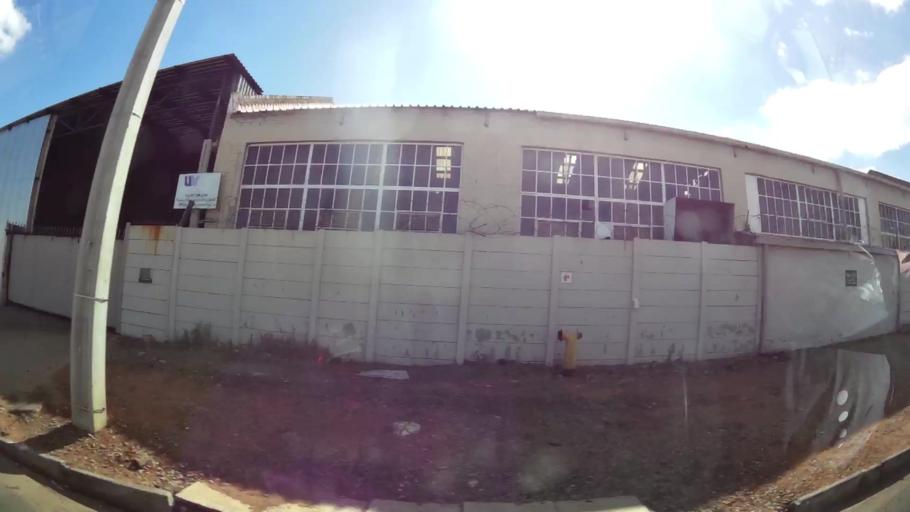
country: ZA
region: Gauteng
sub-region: West Rand District Municipality
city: Krugersdorp
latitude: -26.1174
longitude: 27.8123
